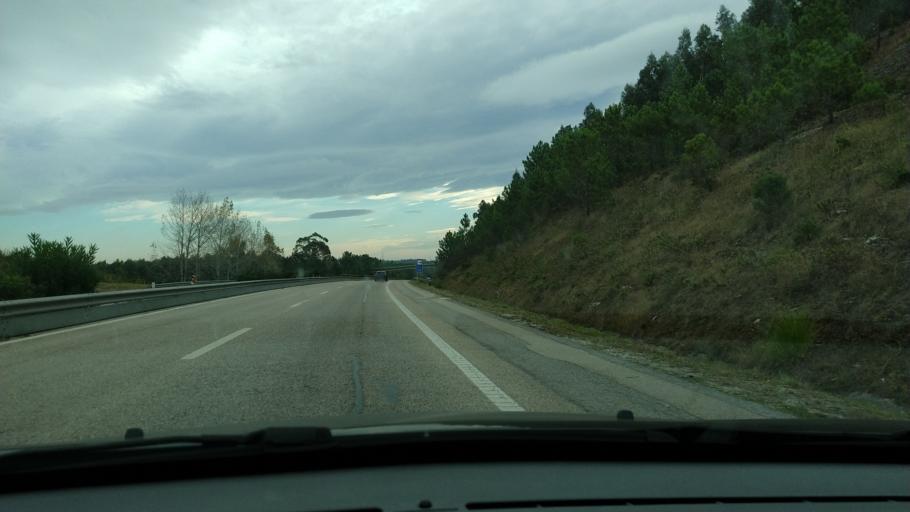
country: PT
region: Coimbra
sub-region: Figueira da Foz
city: Tavarede
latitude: 40.1519
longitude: -8.8128
